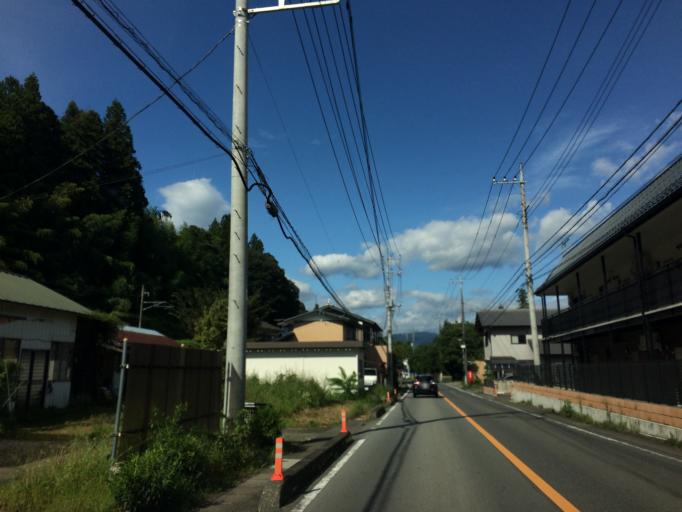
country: JP
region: Gunma
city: Nakanojomachi
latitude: 36.5638
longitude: 138.8164
